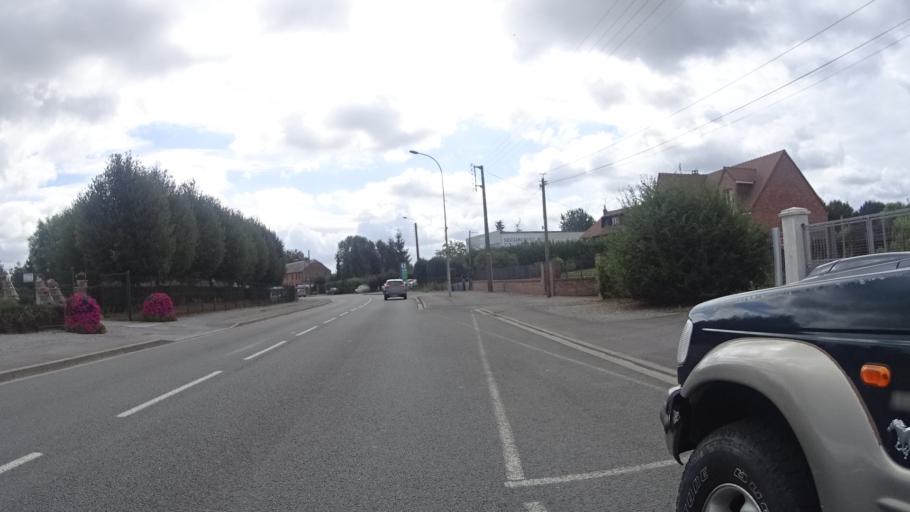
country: FR
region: Nord-Pas-de-Calais
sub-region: Departement du Nord
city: Landrecies
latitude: 50.1200
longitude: 3.6970
